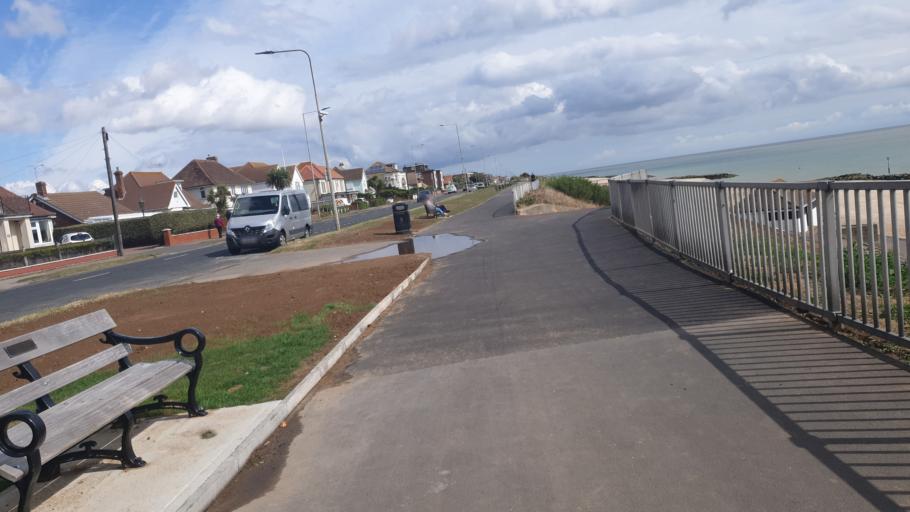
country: GB
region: England
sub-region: Essex
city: Clacton-on-Sea
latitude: 51.7985
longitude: 1.1863
